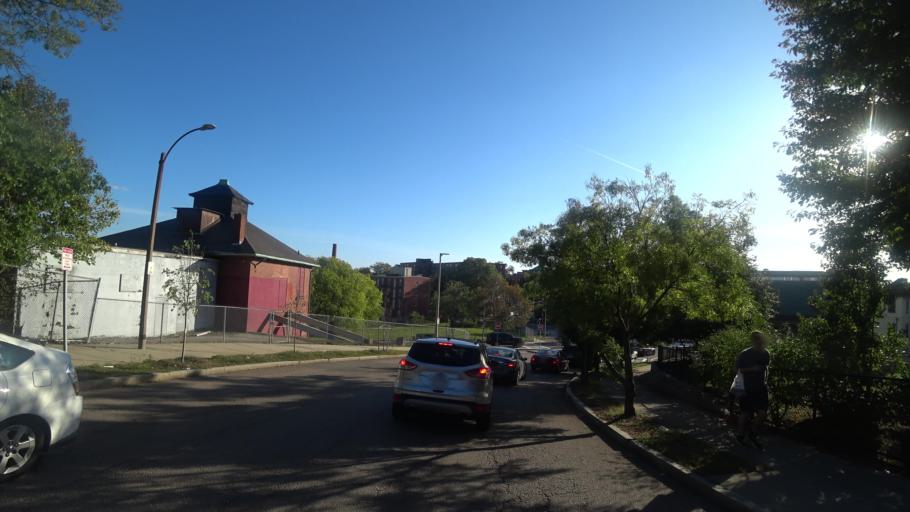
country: US
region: Massachusetts
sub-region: Norfolk County
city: Brookline
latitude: 42.3268
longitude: -71.0997
